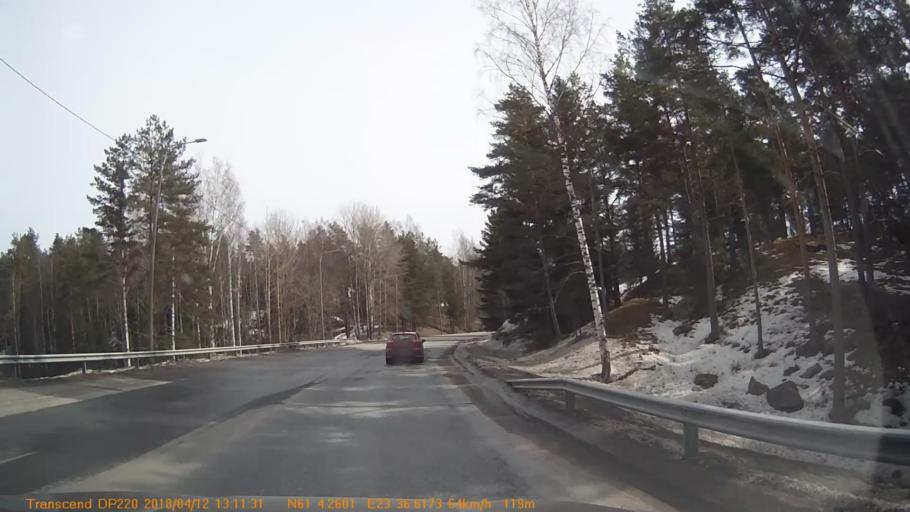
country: FI
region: Pirkanmaa
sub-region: Etelae-Pirkanmaa
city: Urjala
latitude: 61.0708
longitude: 23.6118
